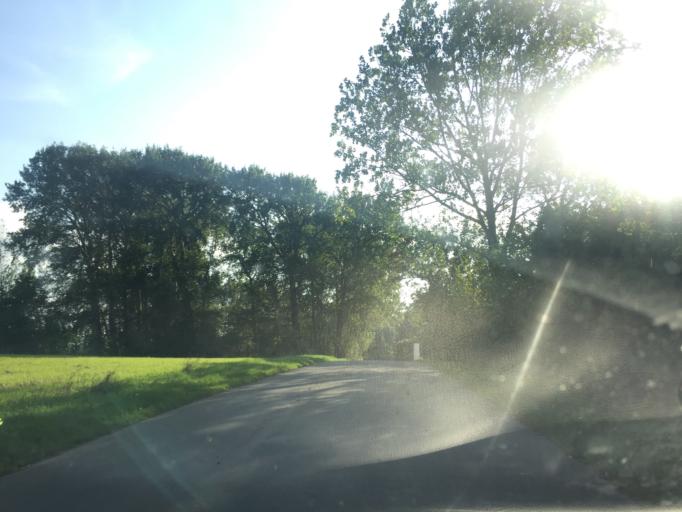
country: DK
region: Zealand
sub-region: Kalundborg Kommune
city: Svebolle
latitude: 55.6590
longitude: 11.2468
